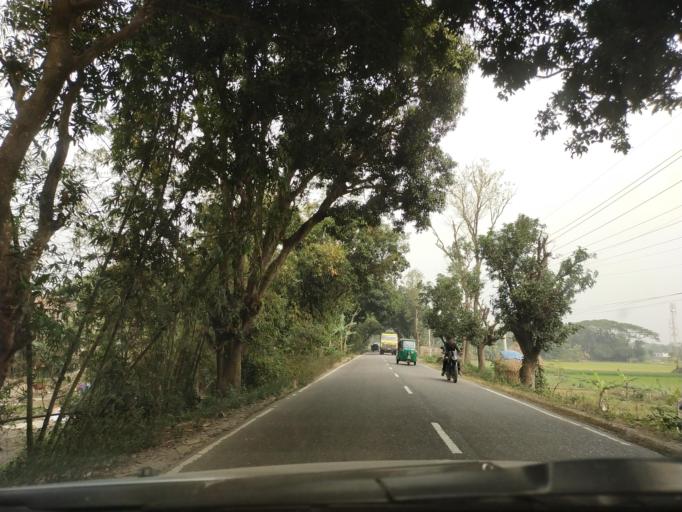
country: BD
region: Dhaka
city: Narsingdi
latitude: 24.0053
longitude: 90.7374
